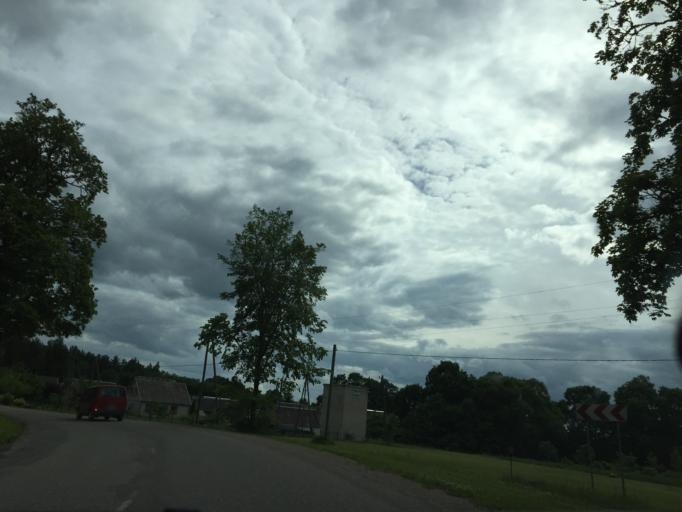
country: LV
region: Apes Novads
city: Ape
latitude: 57.5084
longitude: 26.3995
